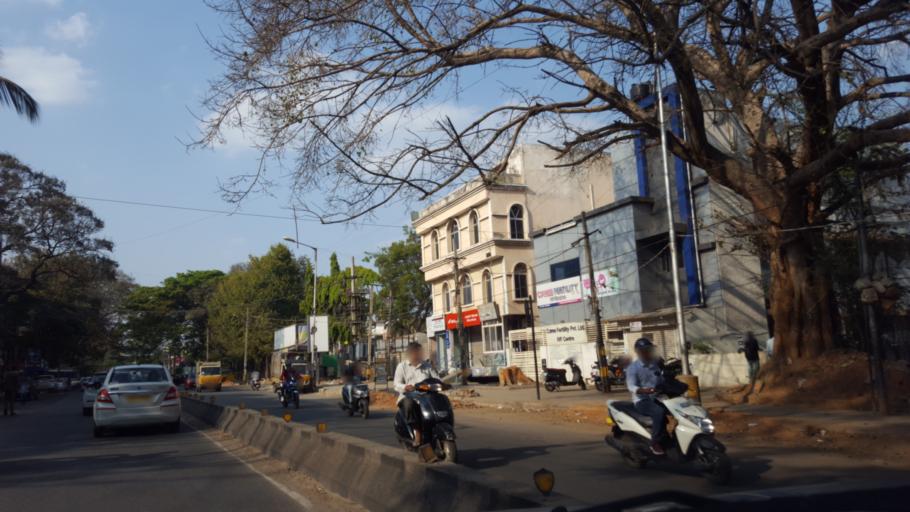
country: IN
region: Karnataka
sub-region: Bangalore Urban
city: Bangalore
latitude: 12.9258
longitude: 77.5971
